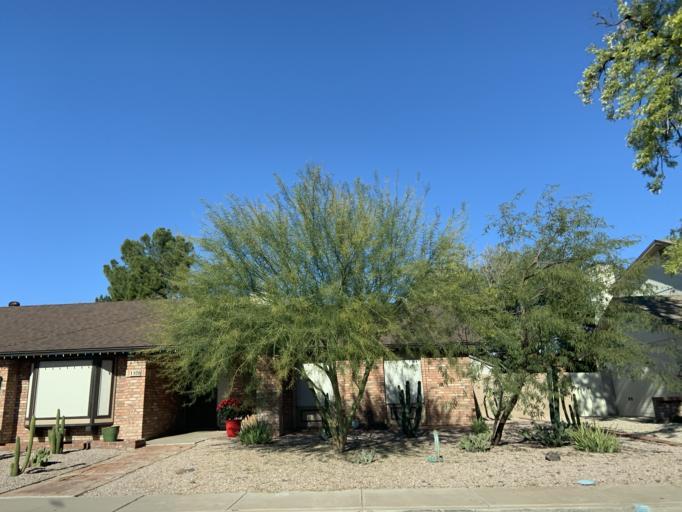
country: US
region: Arizona
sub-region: Maricopa County
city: San Carlos
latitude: 33.3672
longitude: -111.8566
